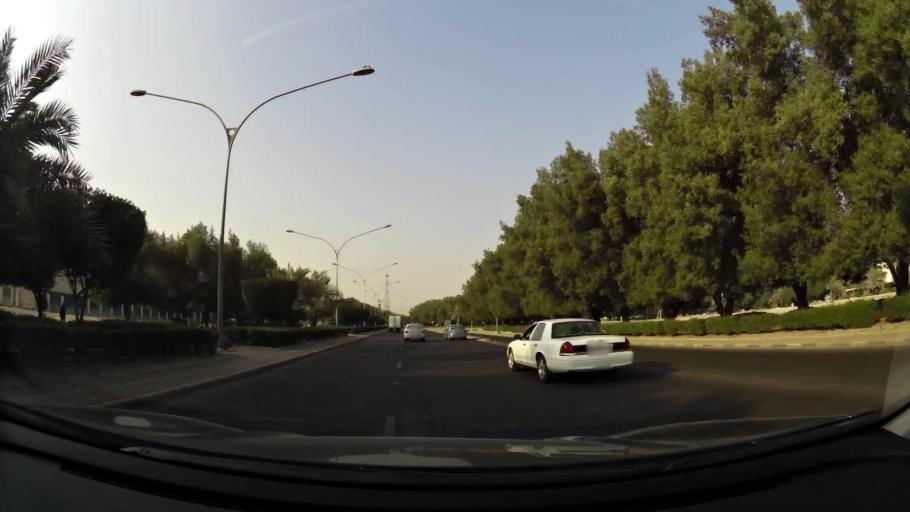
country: KW
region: Muhafazat Hawalli
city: Salwa
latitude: 29.2911
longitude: 48.0659
